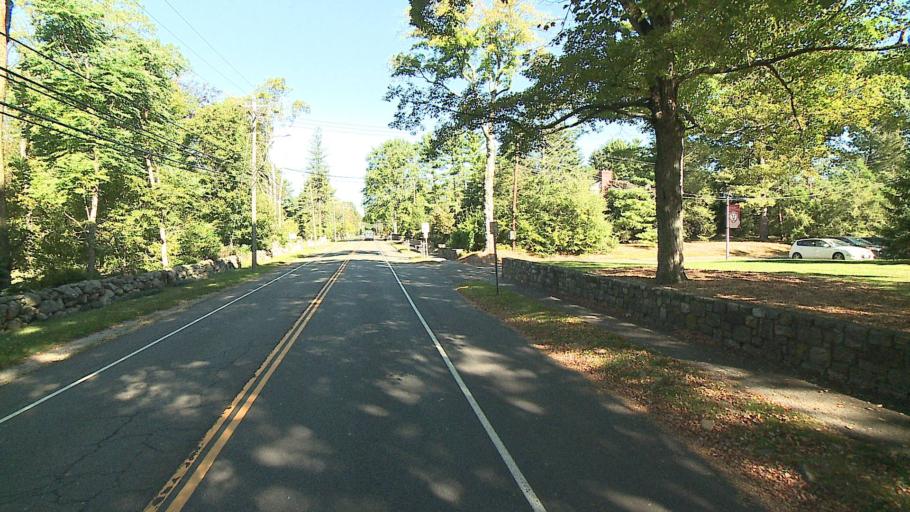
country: US
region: Connecticut
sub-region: Fairfield County
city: New Canaan
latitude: 41.1527
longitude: -73.4990
